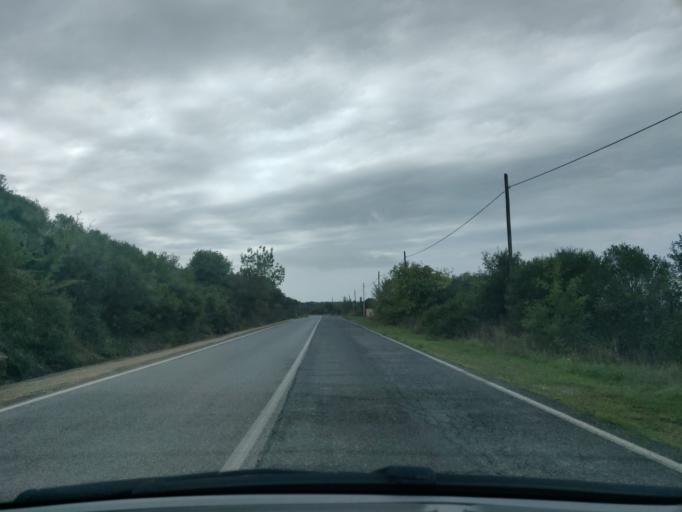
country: IT
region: Latium
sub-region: Citta metropolitana di Roma Capitale
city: Allumiere
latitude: 42.1211
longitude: 11.8629
